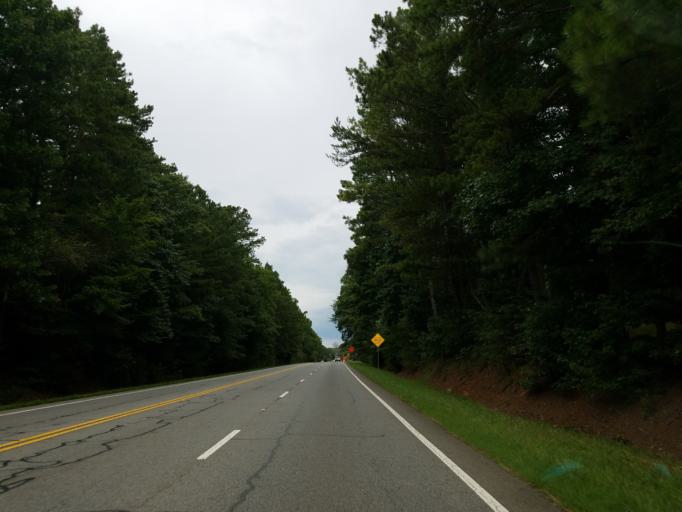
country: US
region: Georgia
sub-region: Bartow County
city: Adairsville
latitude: 34.2786
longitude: -84.8682
